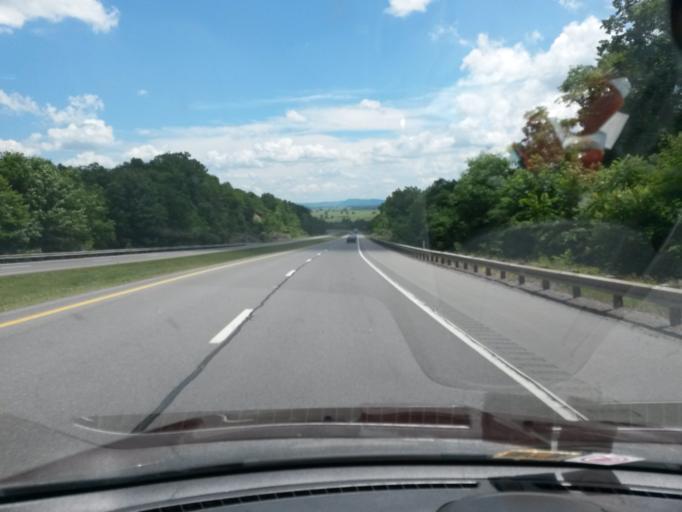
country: US
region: West Virginia
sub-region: Greenbrier County
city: Lewisburg
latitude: 37.8567
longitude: -80.5124
